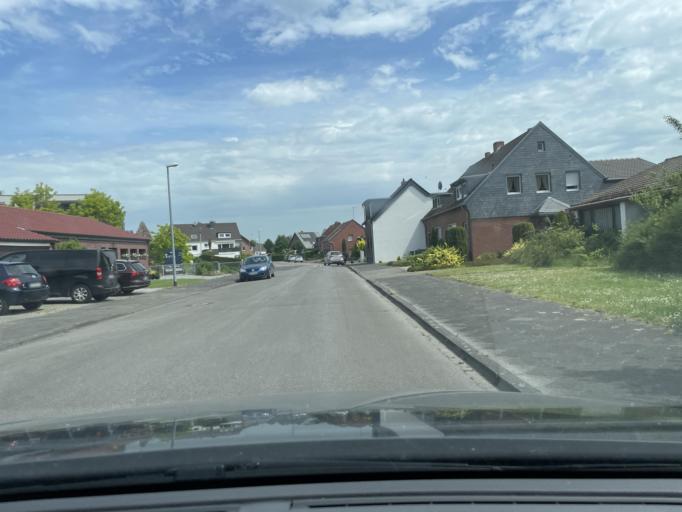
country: DE
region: North Rhine-Westphalia
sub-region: Regierungsbezirk Dusseldorf
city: Schwalmtal
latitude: 51.2060
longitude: 6.3335
